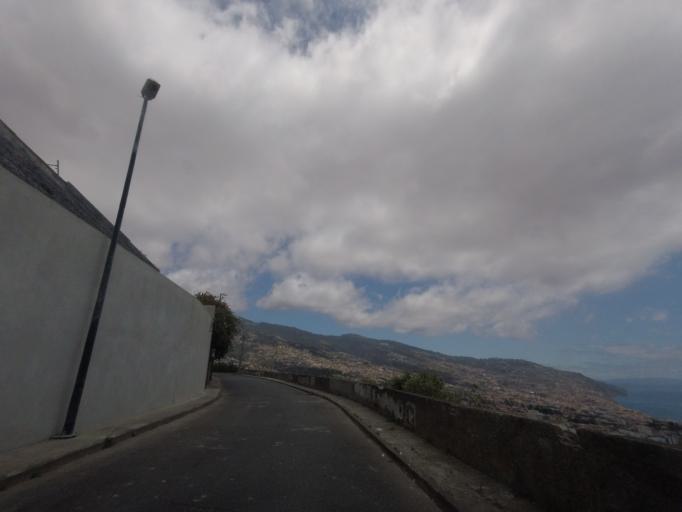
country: PT
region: Madeira
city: Camara de Lobos
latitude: 32.6570
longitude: -16.9393
